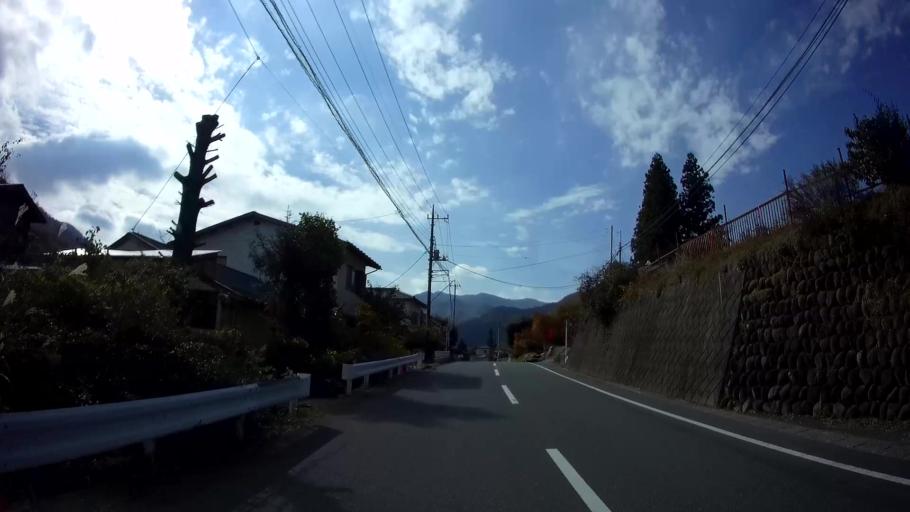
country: JP
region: Gunma
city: Nakanojomachi
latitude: 36.5027
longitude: 138.6908
